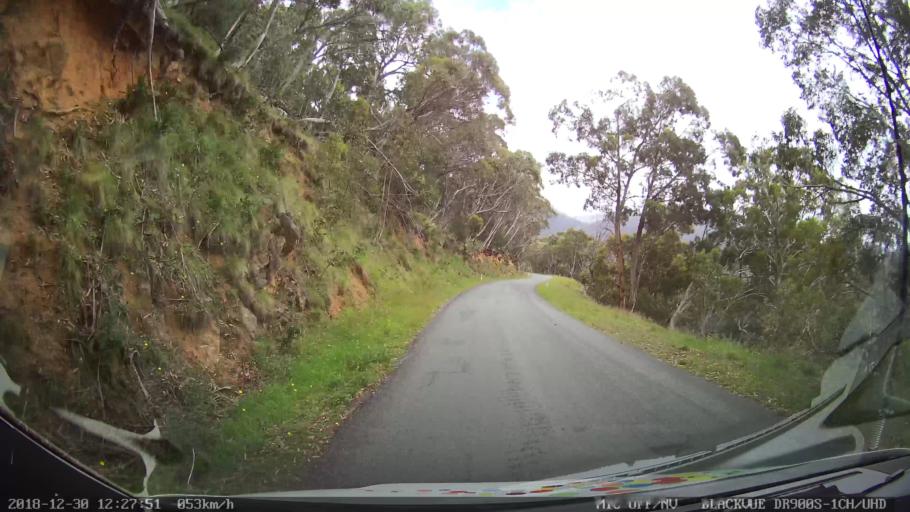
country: AU
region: New South Wales
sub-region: Snowy River
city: Jindabyne
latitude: -36.3282
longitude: 148.4889
